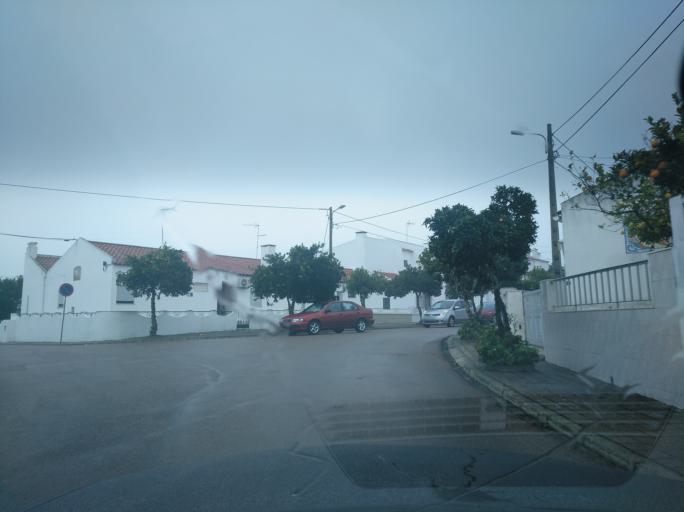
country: PT
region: Portalegre
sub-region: Campo Maior
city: Campo Maior
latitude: 39.0185
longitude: -7.0667
